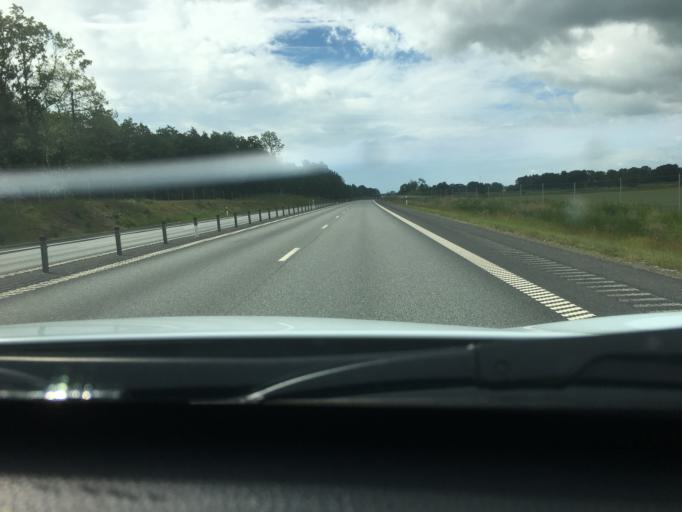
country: SE
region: Blekinge
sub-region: Karlshamns Kommun
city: Morrum
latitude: 56.1489
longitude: 14.6639
